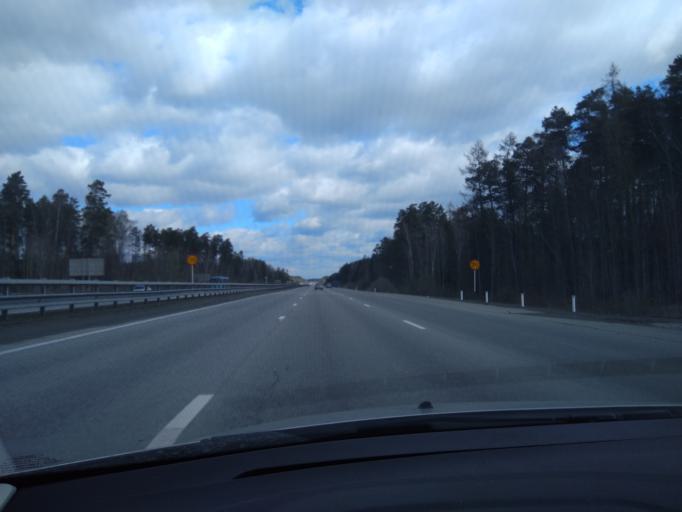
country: RU
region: Sverdlovsk
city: Shuvakish
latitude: 56.9473
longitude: 60.5136
